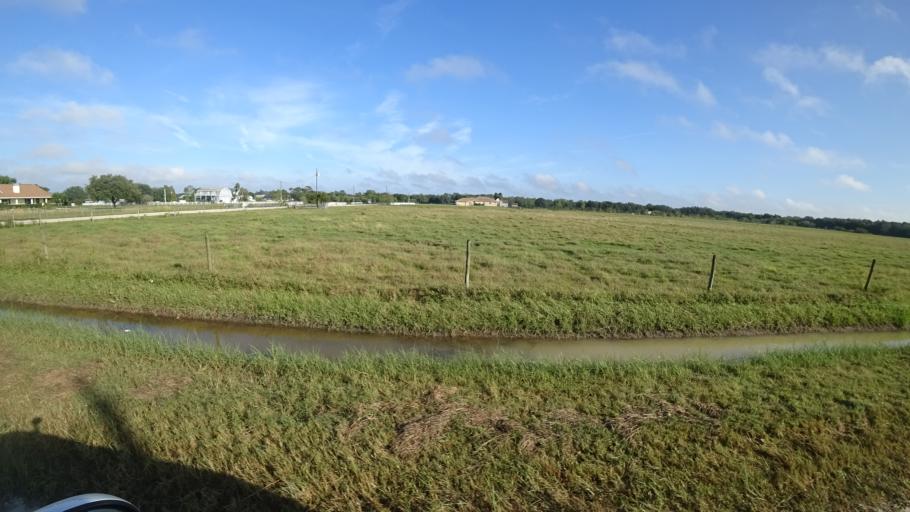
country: US
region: Florida
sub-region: Sarasota County
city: The Meadows
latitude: 27.4311
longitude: -82.3114
